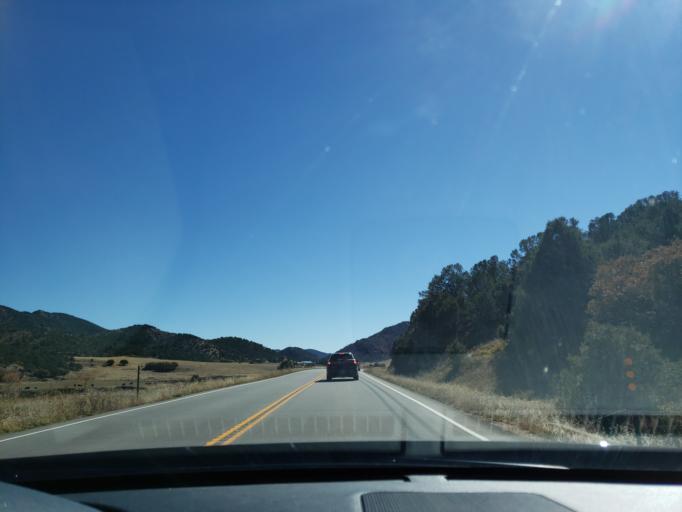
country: US
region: Colorado
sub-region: Fremont County
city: Canon City
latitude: 38.5960
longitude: -105.4262
